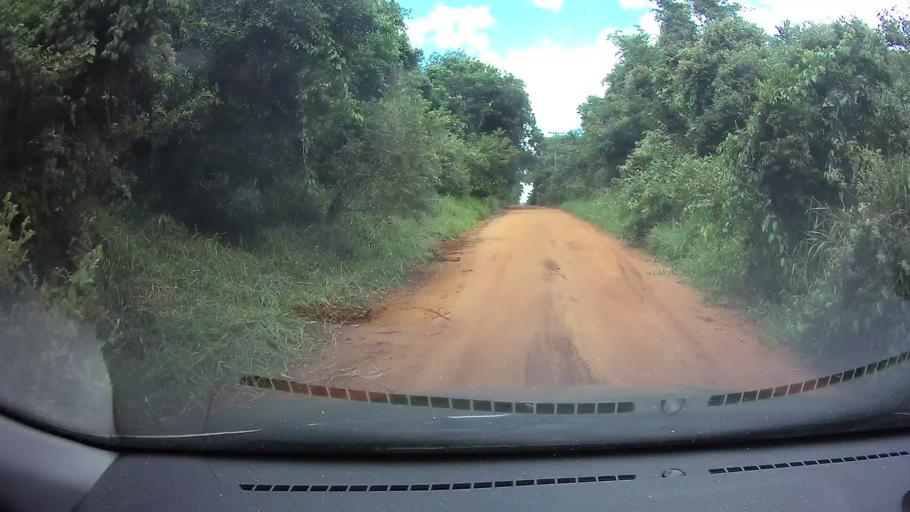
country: PY
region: Paraguari
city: La Colmena
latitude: -25.9452
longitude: -56.7803
